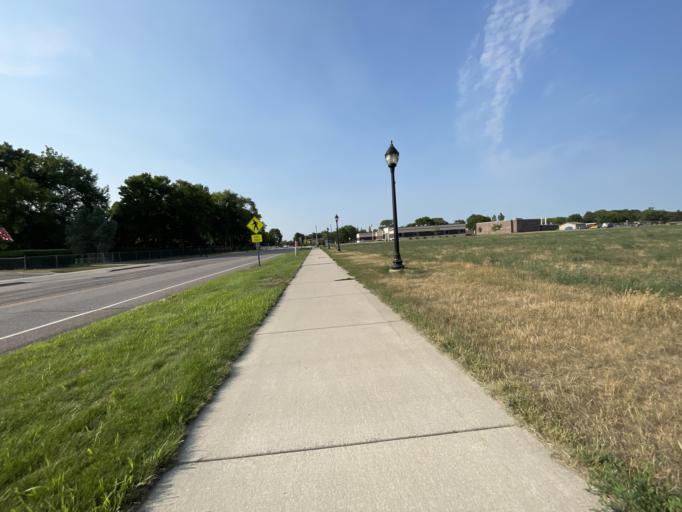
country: US
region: Minnesota
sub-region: Stearns County
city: Saint Joseph
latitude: 45.5605
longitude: -94.3167
